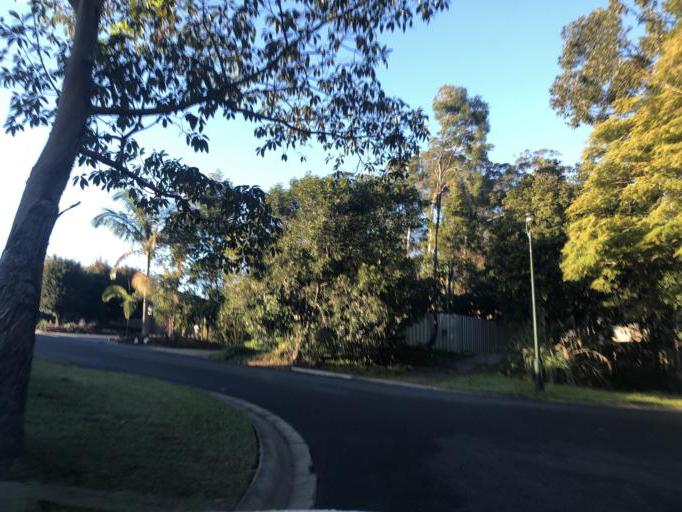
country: AU
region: New South Wales
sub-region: Coffs Harbour
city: Coffs Harbour
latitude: -30.2949
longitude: 153.1291
